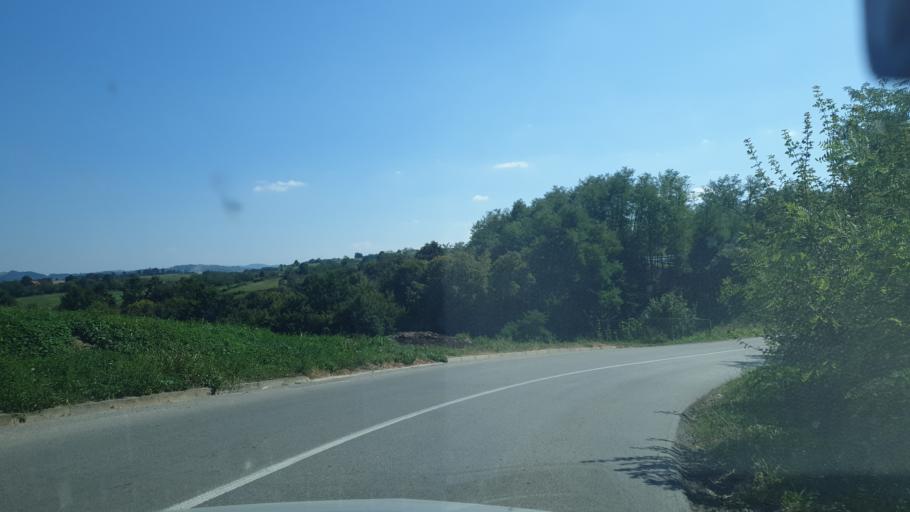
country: RS
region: Central Serbia
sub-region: Kolubarski Okrug
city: Mionica
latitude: 44.1955
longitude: 20.0262
